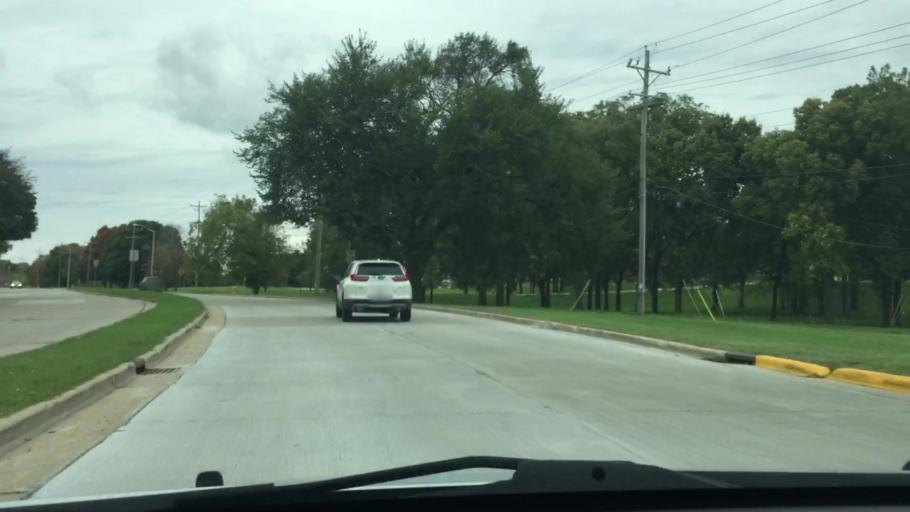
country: US
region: Wisconsin
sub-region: Waukesha County
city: Waukesha
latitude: 43.0322
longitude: -88.2453
